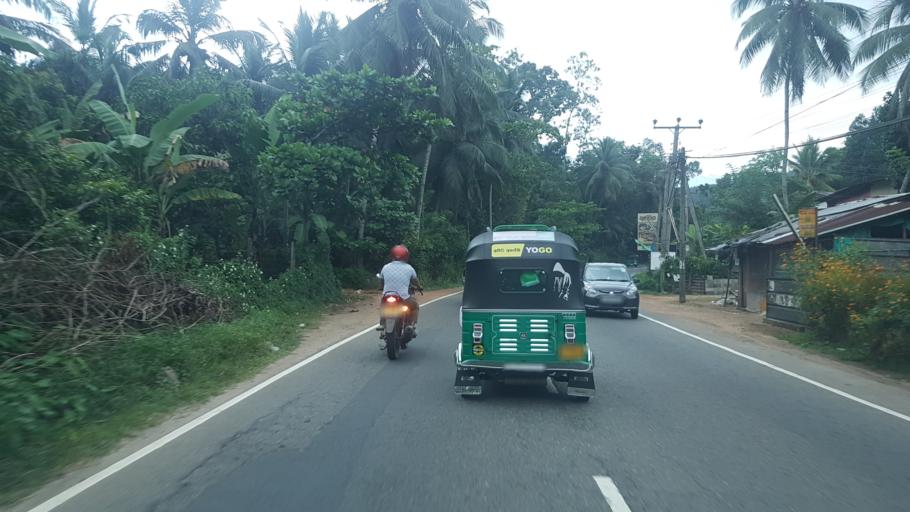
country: LK
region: Western
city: Hanwella Ihala
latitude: 7.0107
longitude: 80.2622
